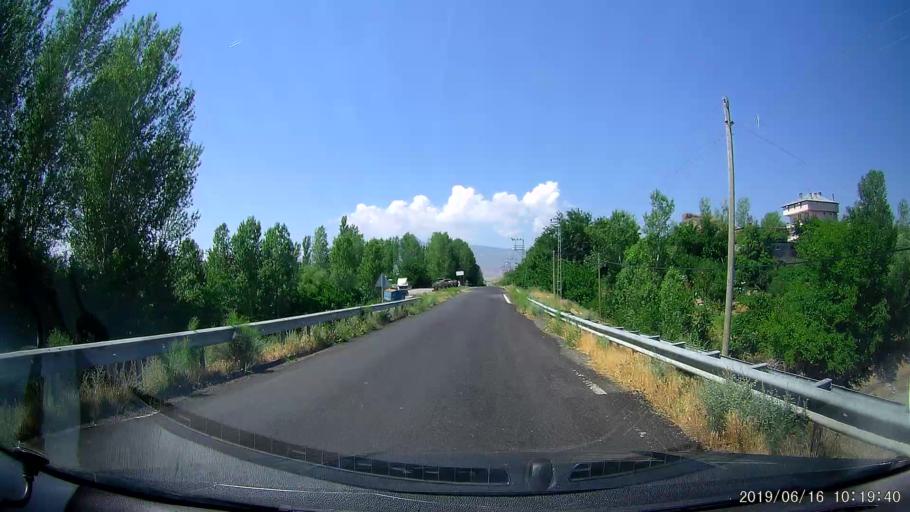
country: TR
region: Igdir
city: Tuzluca
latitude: 40.1536
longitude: 43.6545
